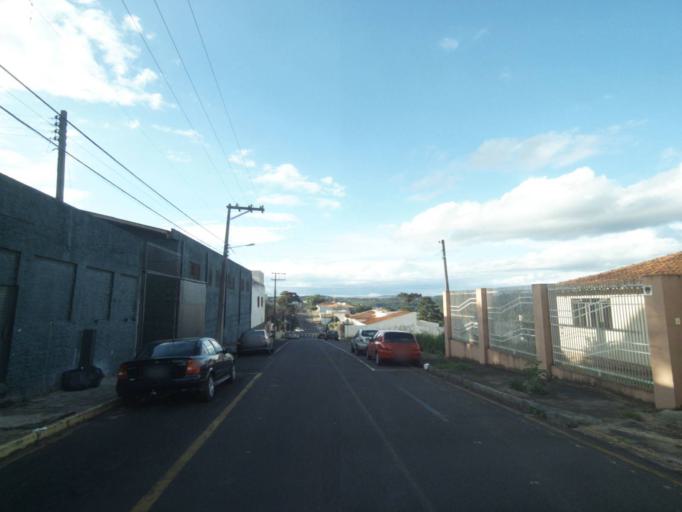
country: BR
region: Parana
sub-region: Telemaco Borba
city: Telemaco Borba
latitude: -24.3255
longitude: -50.6162
